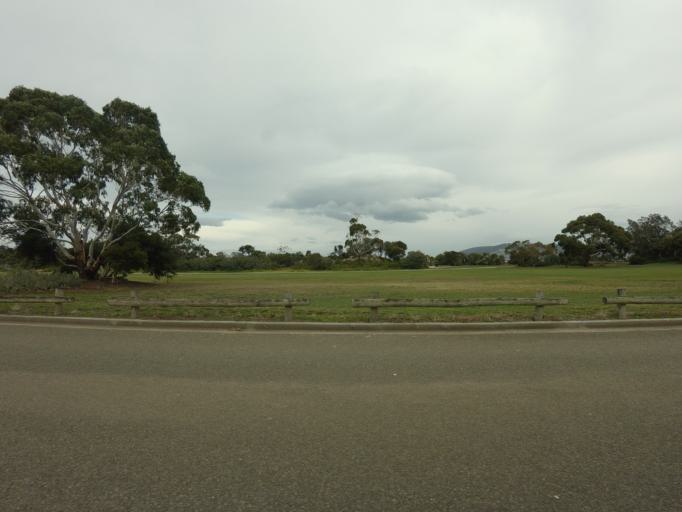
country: AU
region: Tasmania
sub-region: Clarence
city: Howrah
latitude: -42.8805
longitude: 147.3966
